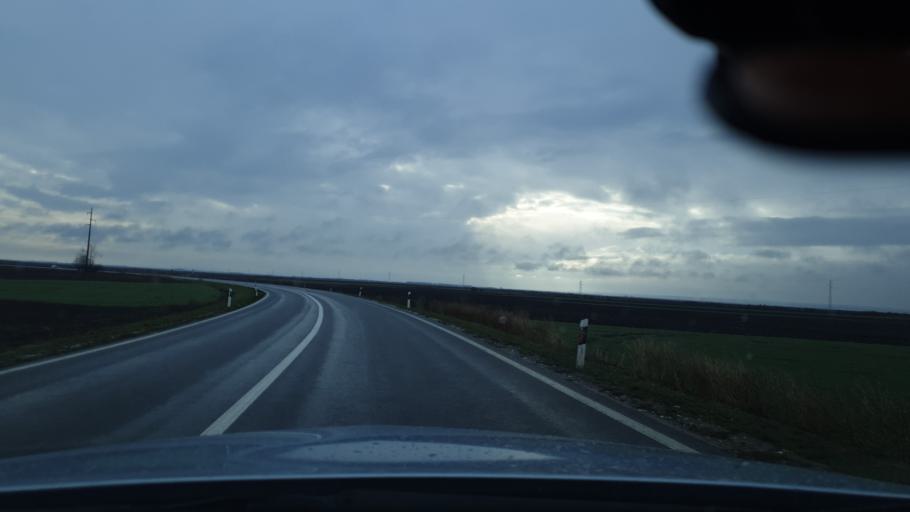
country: RS
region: Autonomna Pokrajina Vojvodina
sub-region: Juznobanatski Okrug
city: Kovin
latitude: 44.8116
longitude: 20.8578
